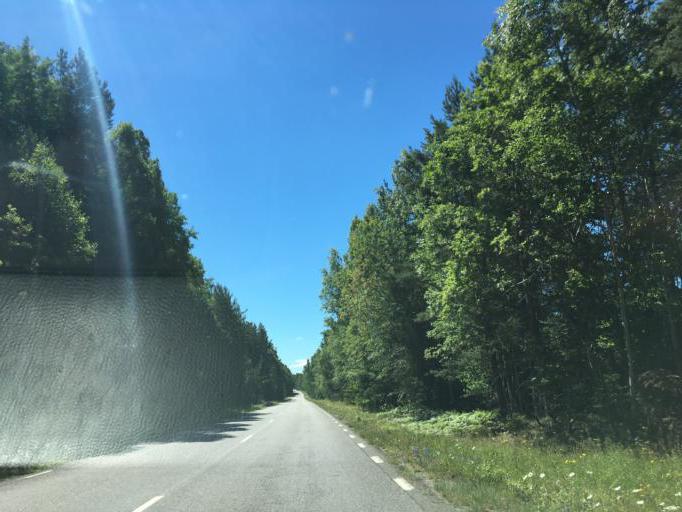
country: SE
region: OErebro
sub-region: Laxa Kommun
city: Laxa
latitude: 58.8410
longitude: 14.5476
